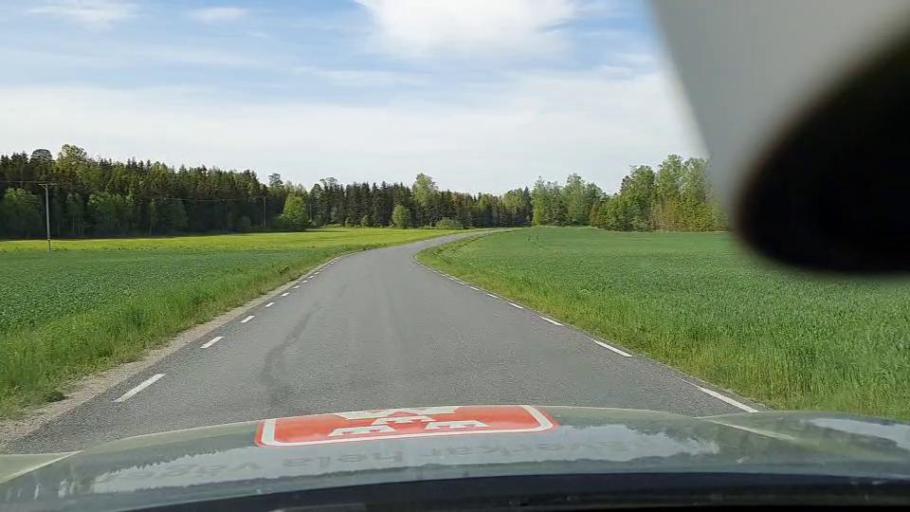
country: SE
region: Soedermanland
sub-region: Eskilstuna Kommun
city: Arla
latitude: 59.2745
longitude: 16.6673
